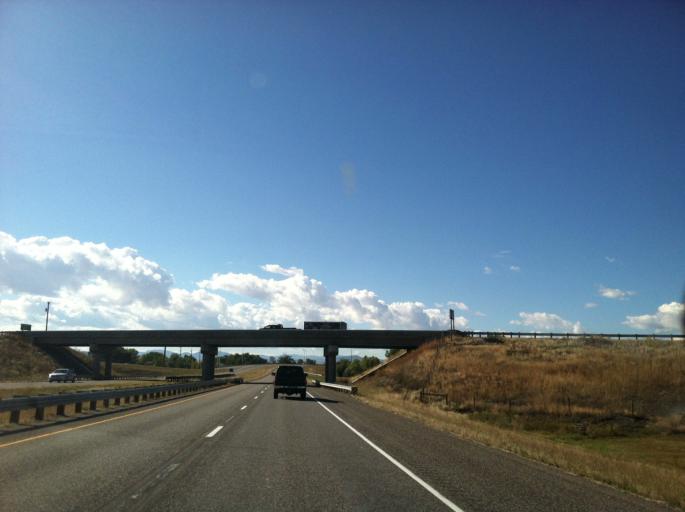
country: US
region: Montana
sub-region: Gallatin County
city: Three Forks
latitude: 45.9014
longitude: -111.5330
